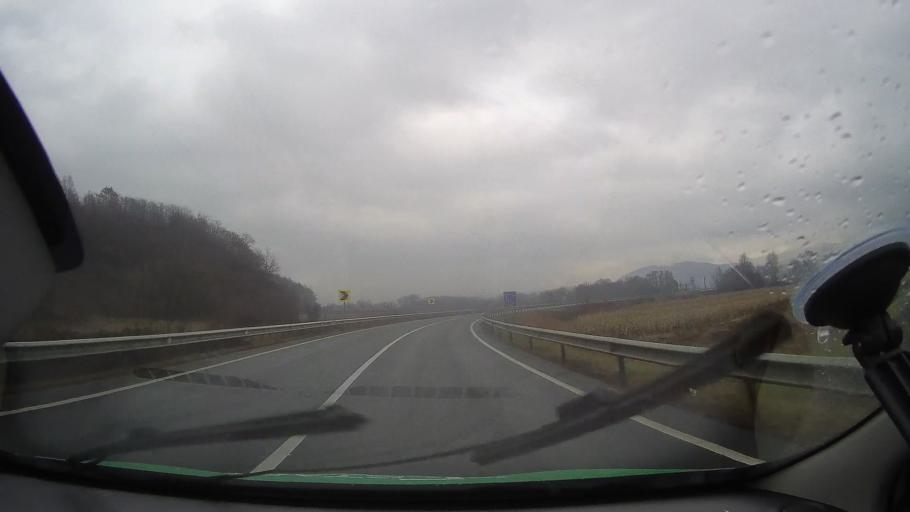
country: RO
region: Hunedoara
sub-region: Comuna Tomesti
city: Tomesti
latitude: 46.1841
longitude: 22.6563
